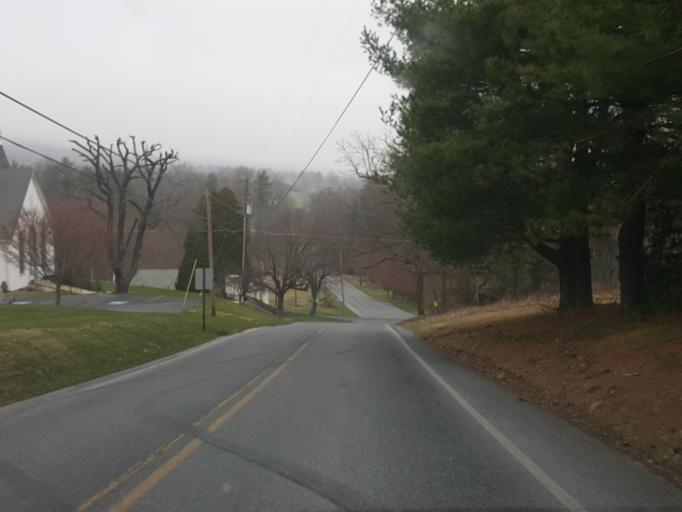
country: US
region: Pennsylvania
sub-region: Schuylkill County
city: Tower City
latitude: 40.5356
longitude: -76.4802
